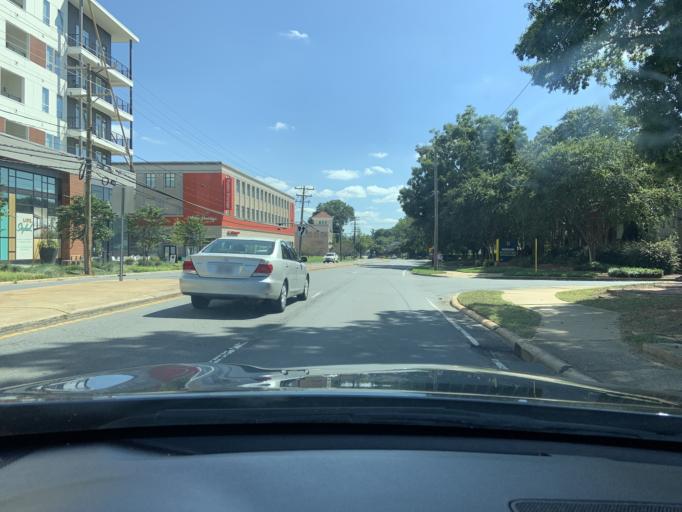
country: US
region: North Carolina
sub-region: Mecklenburg County
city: Charlotte
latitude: 35.1670
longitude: -80.8506
